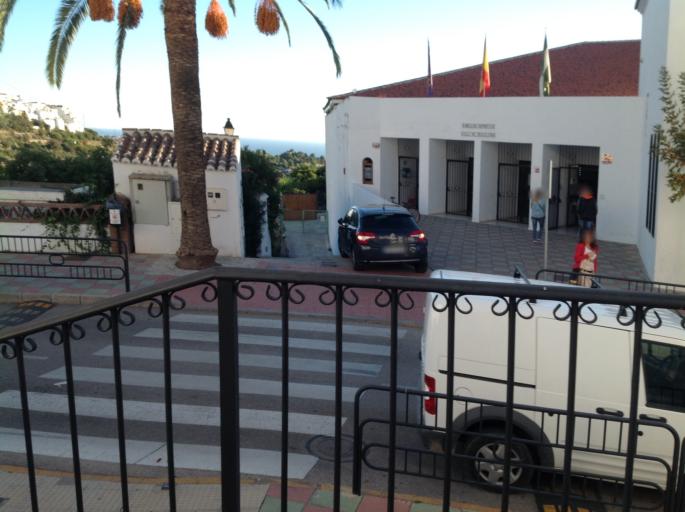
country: ES
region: Andalusia
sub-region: Provincia de Malaga
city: Frigiliana
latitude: 36.7916
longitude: -3.8985
